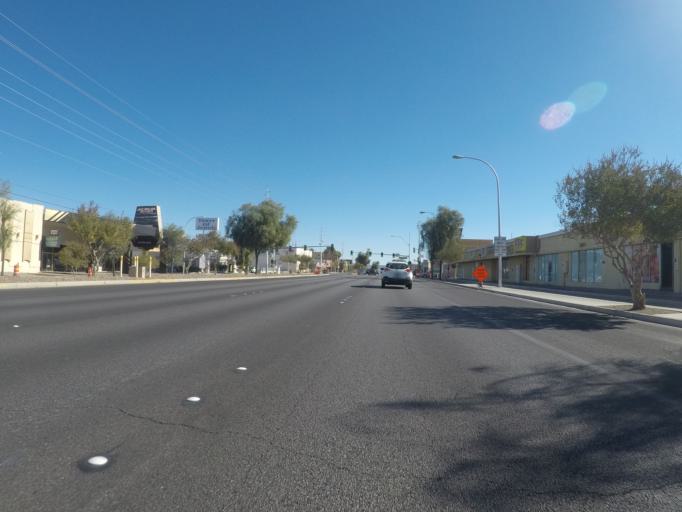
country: US
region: Nevada
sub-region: Clark County
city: Winchester
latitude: 36.1439
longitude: -115.1436
